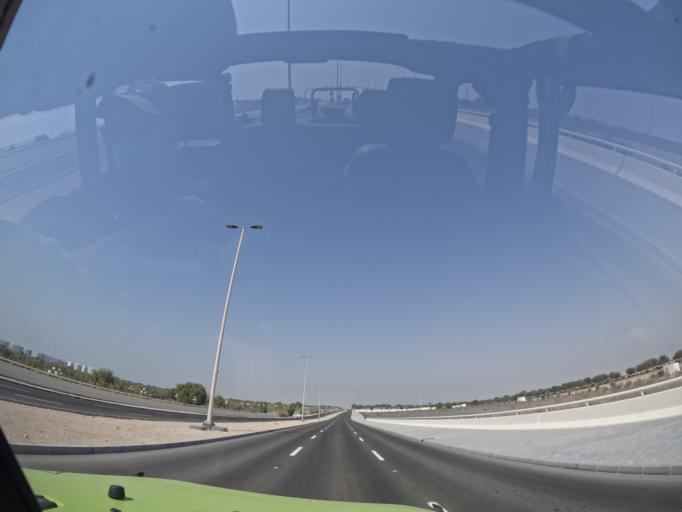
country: AE
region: Abu Dhabi
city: Abu Dhabi
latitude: 24.4661
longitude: 54.6260
